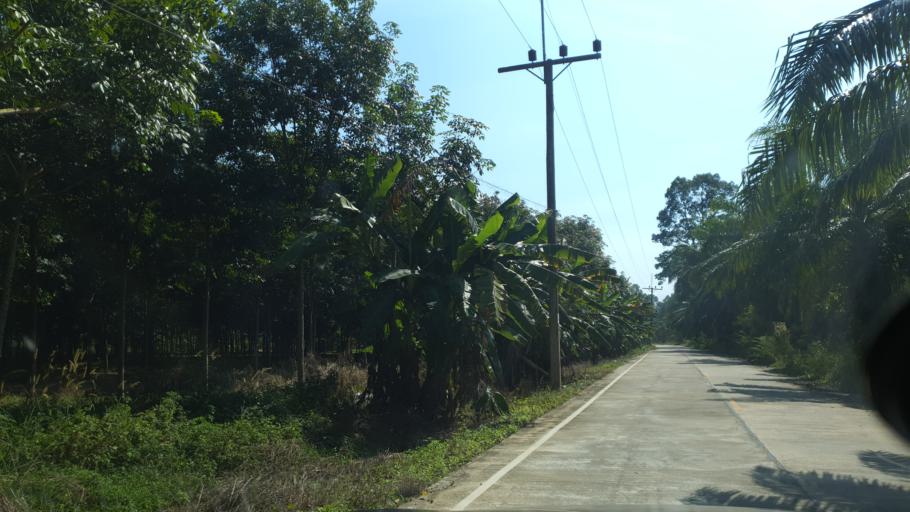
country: TH
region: Surat Thani
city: Tha Chana
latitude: 9.5911
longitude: 99.2019
